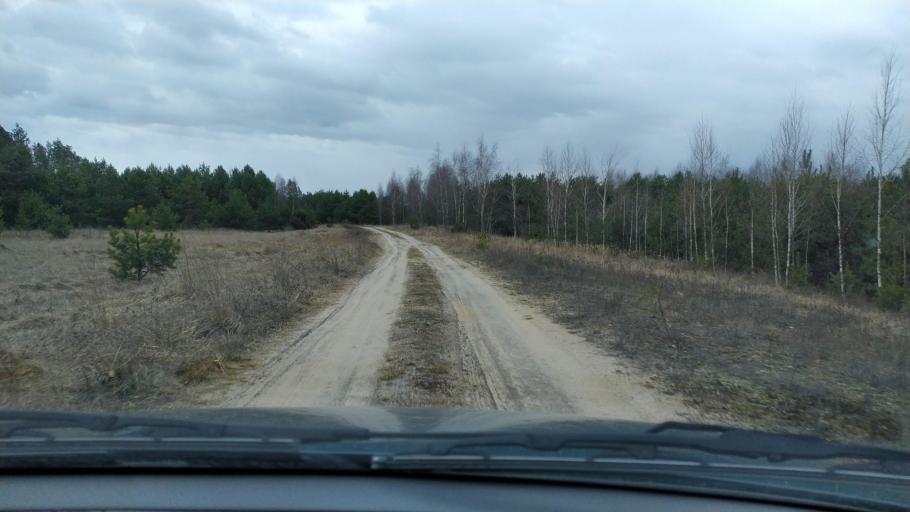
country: BY
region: Brest
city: Zhabinka
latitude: 52.4013
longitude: 24.0682
